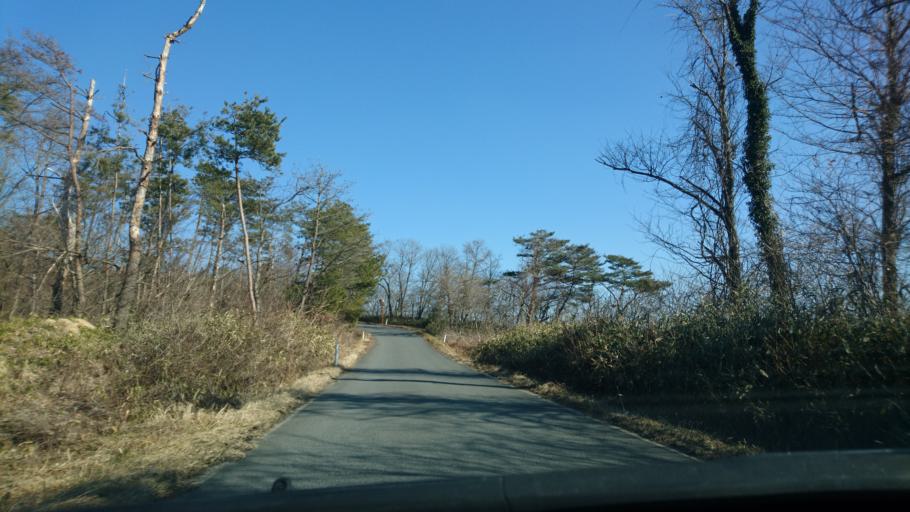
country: JP
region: Iwate
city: Ichinoseki
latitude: 38.8454
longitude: 141.2309
